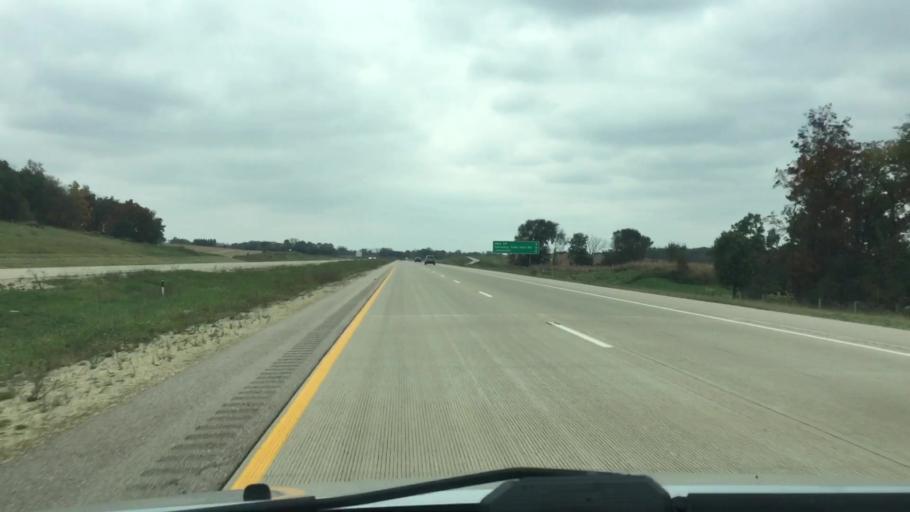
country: US
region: Wisconsin
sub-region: Rock County
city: Milton
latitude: 42.8117
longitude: -88.9269
